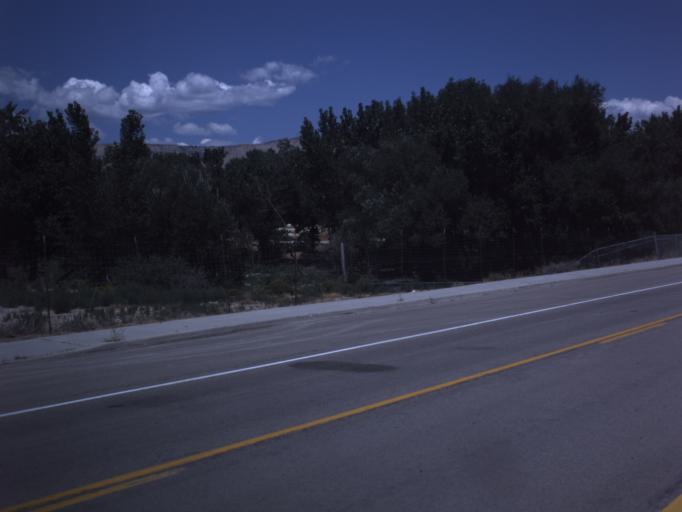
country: US
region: Utah
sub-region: Emery County
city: Ferron
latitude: 39.0814
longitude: -111.1318
